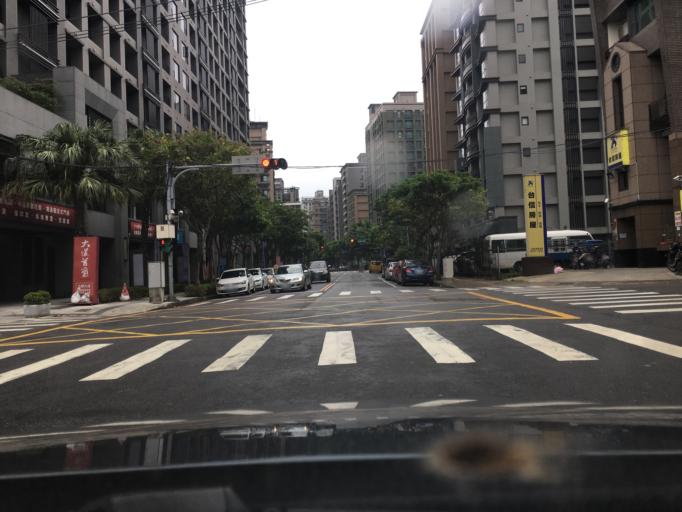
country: TW
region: Taipei
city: Taipei
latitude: 25.0875
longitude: 121.4850
